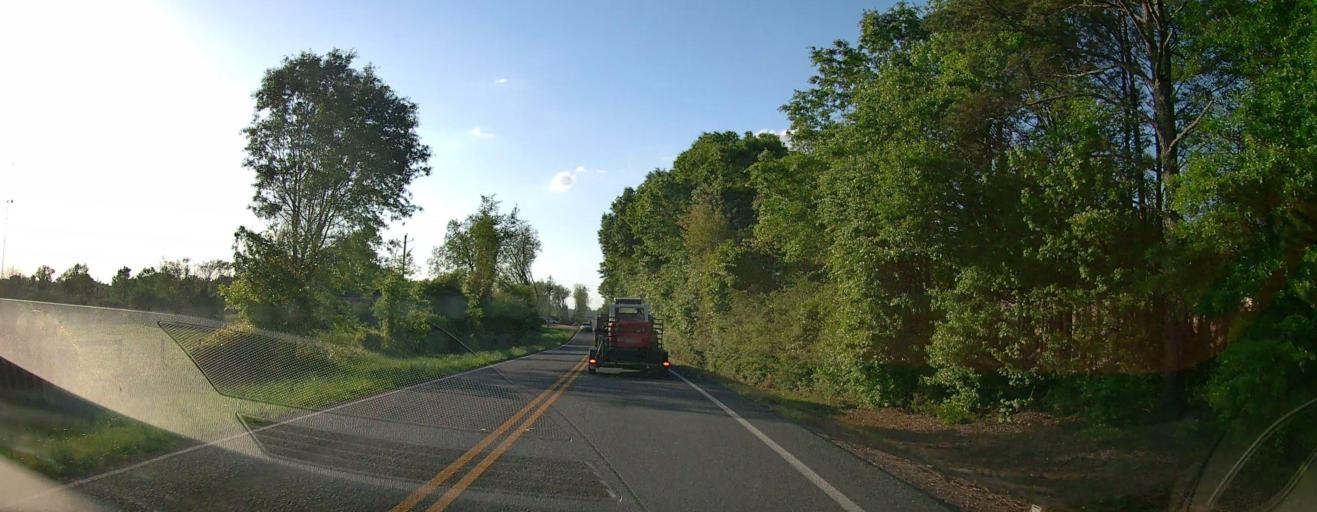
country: US
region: Georgia
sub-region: Jasper County
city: Monticello
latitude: 33.4413
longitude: -83.6213
